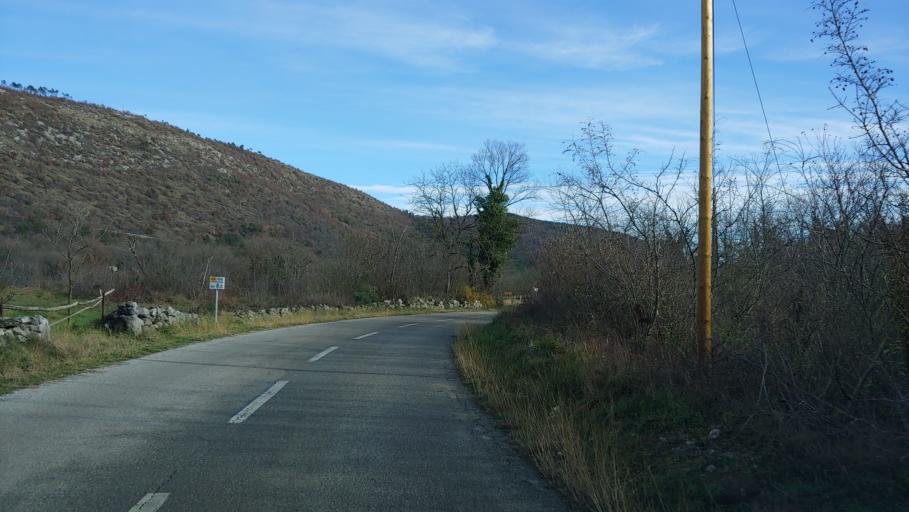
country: IT
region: Friuli Venezia Giulia
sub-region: Provincia di Trieste
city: Duino
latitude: 45.8129
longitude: 13.6208
